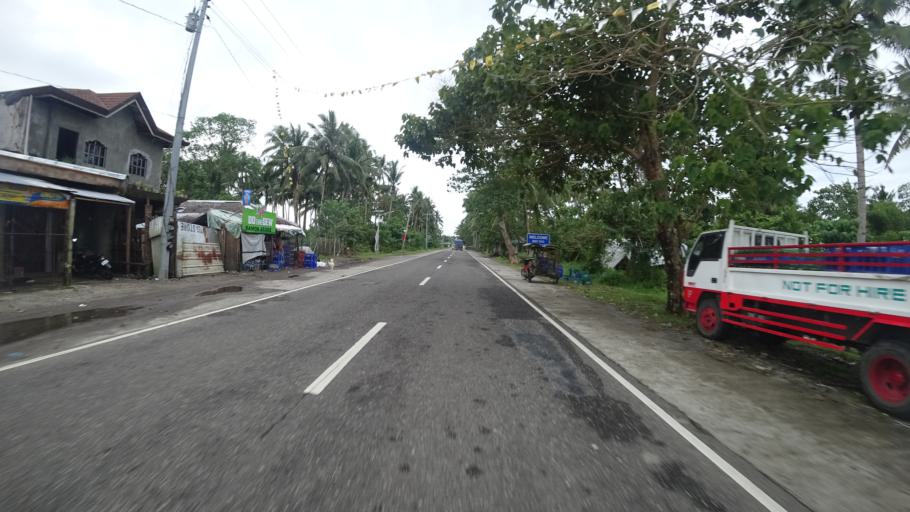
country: PH
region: Eastern Visayas
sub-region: Province of Leyte
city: MacArthur
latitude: 10.8380
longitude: 124.9957
